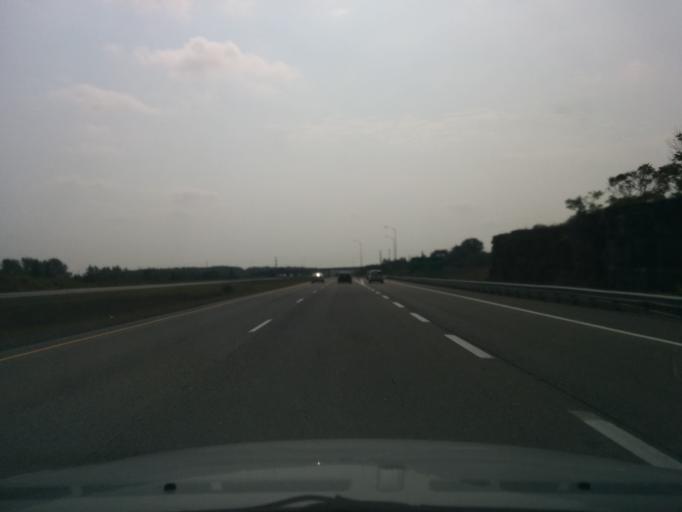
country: CA
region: Ontario
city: Bells Corners
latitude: 45.2757
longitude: -75.8002
